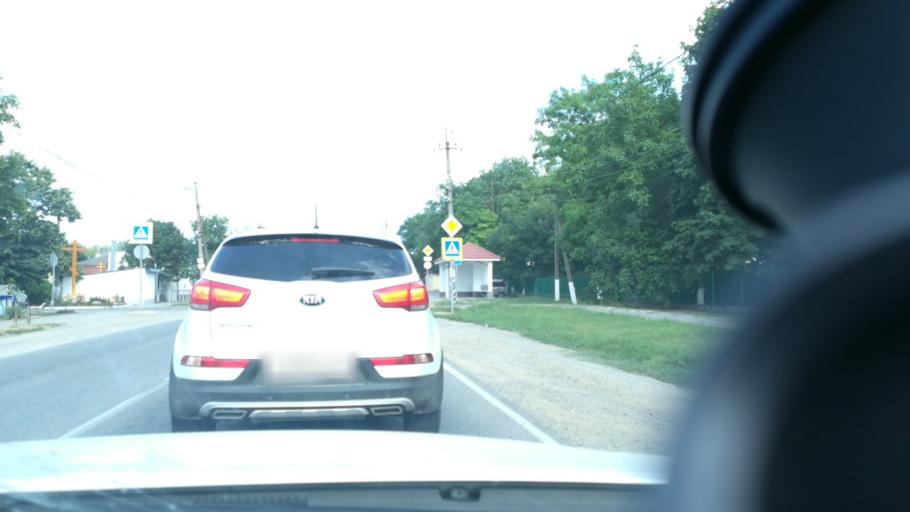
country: RU
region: Krasnodarskiy
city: Gostagayevskaya
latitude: 45.0257
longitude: 37.5011
